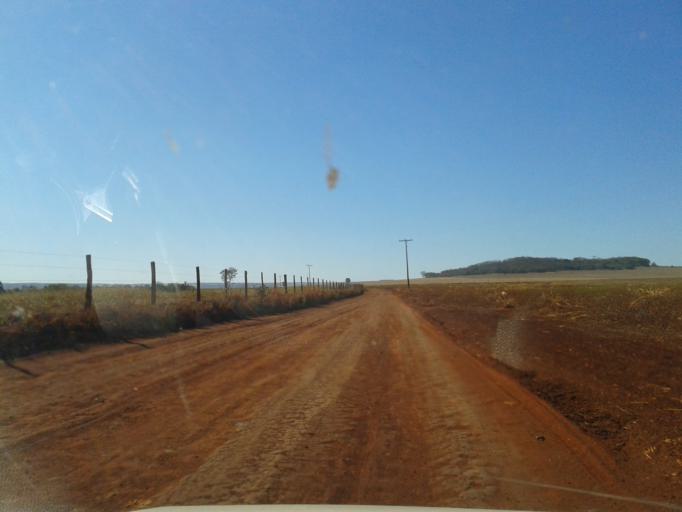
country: BR
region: Minas Gerais
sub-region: Centralina
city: Centralina
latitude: -18.5912
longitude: -49.1726
